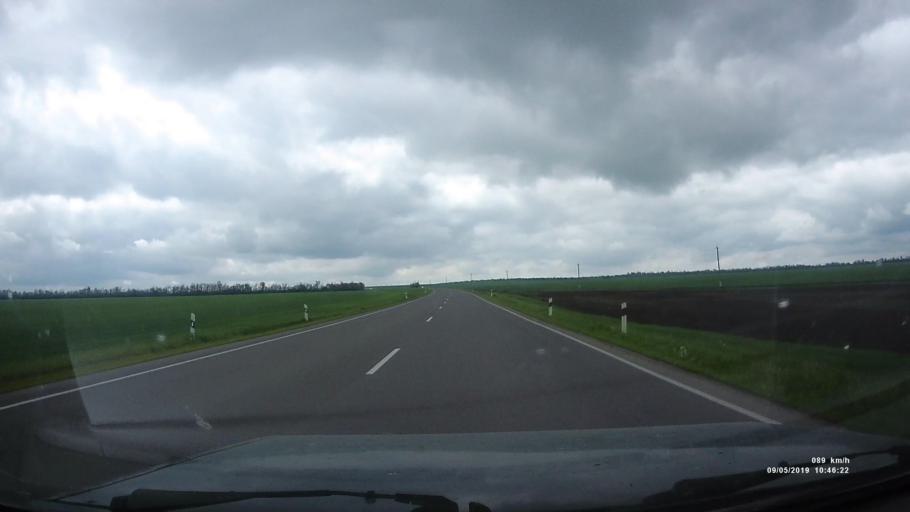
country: RU
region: Rostov
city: Peshkovo
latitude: 46.9854
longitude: 39.3568
